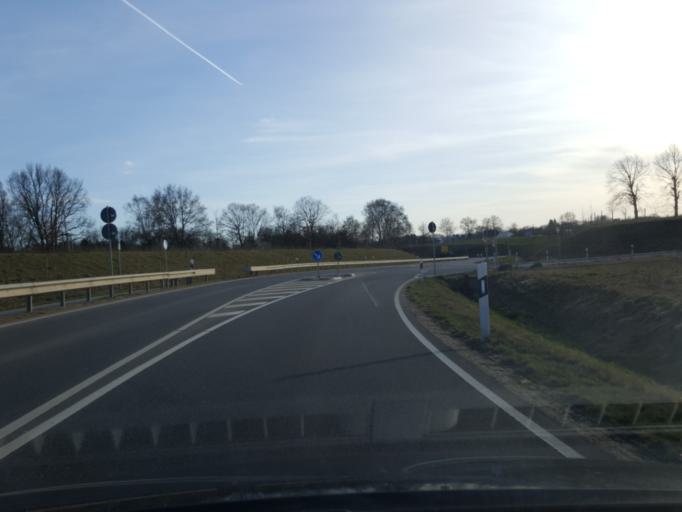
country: DE
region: Lower Saxony
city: Seevetal
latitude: 53.3815
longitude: 9.9701
